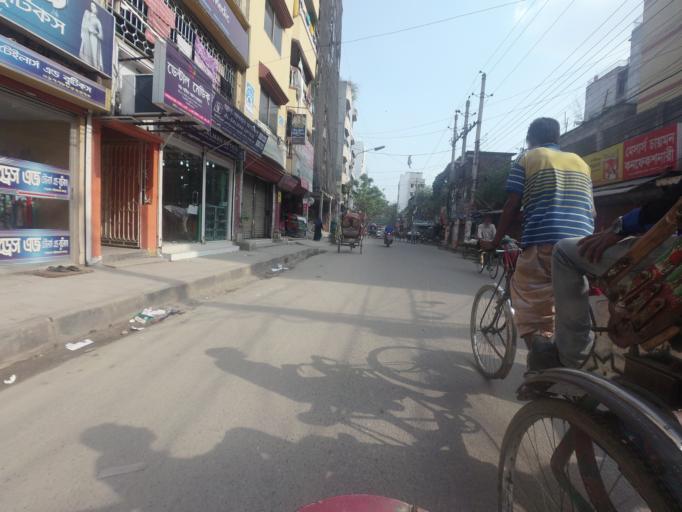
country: BD
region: Dhaka
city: Azimpur
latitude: 23.7598
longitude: 90.3620
